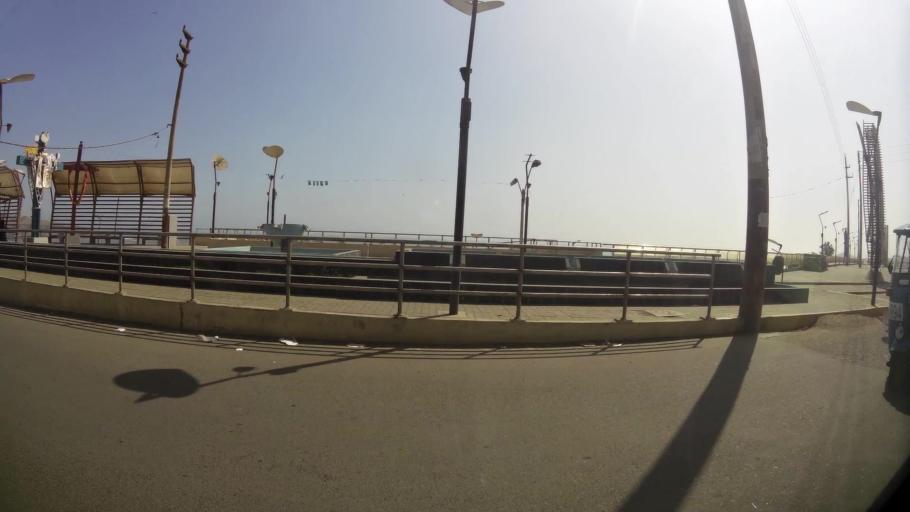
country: PE
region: Lima
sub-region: Huaura
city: Huacho
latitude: -11.1139
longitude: -77.6120
